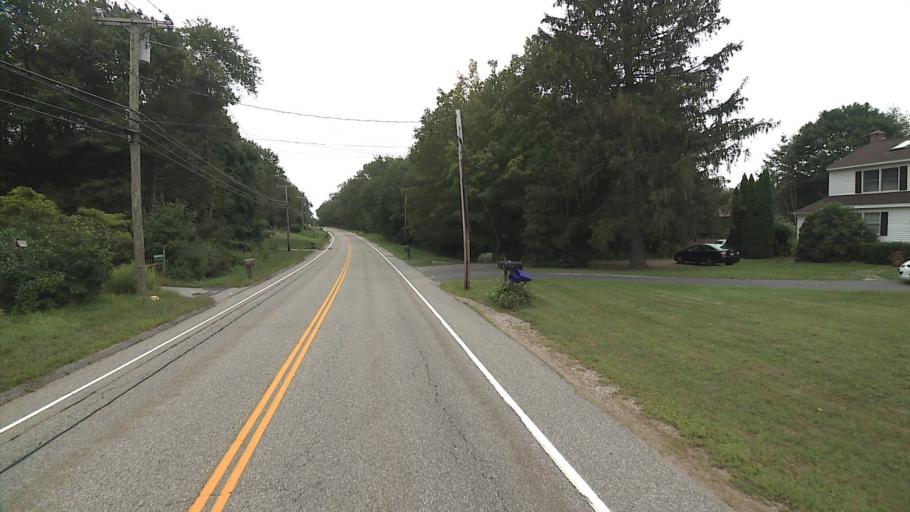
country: US
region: Connecticut
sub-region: Hartford County
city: Manchester
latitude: 41.7679
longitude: -72.4433
